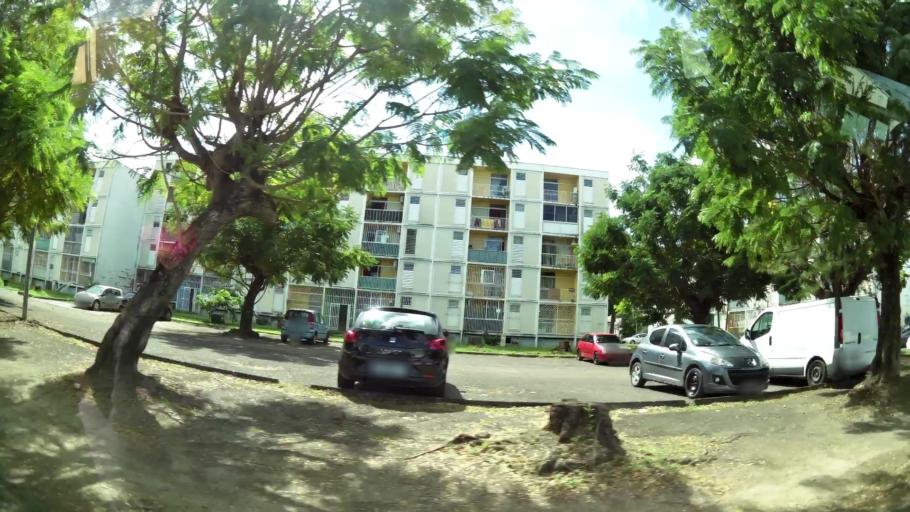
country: GP
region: Guadeloupe
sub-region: Guadeloupe
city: Pointe-a-Pitre
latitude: 16.2557
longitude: -61.5288
